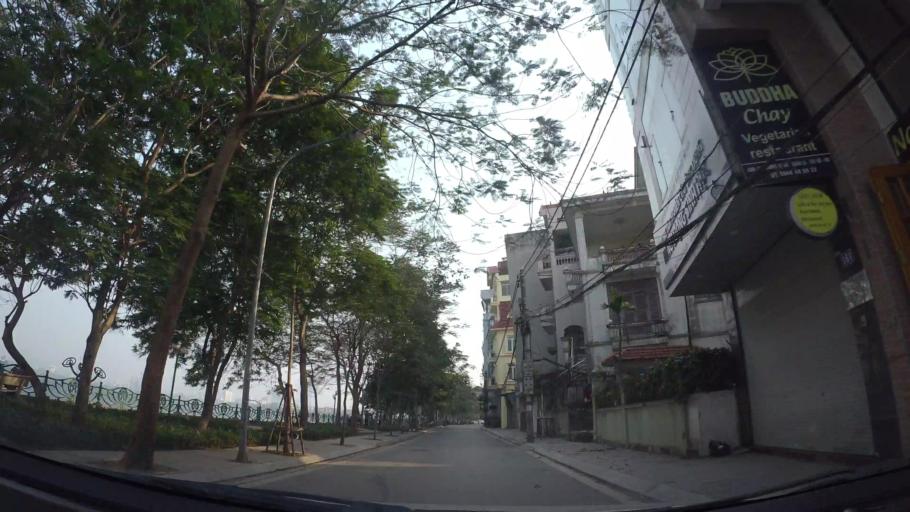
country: VN
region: Ha Noi
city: Tay Ho
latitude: 21.0646
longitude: 105.8106
